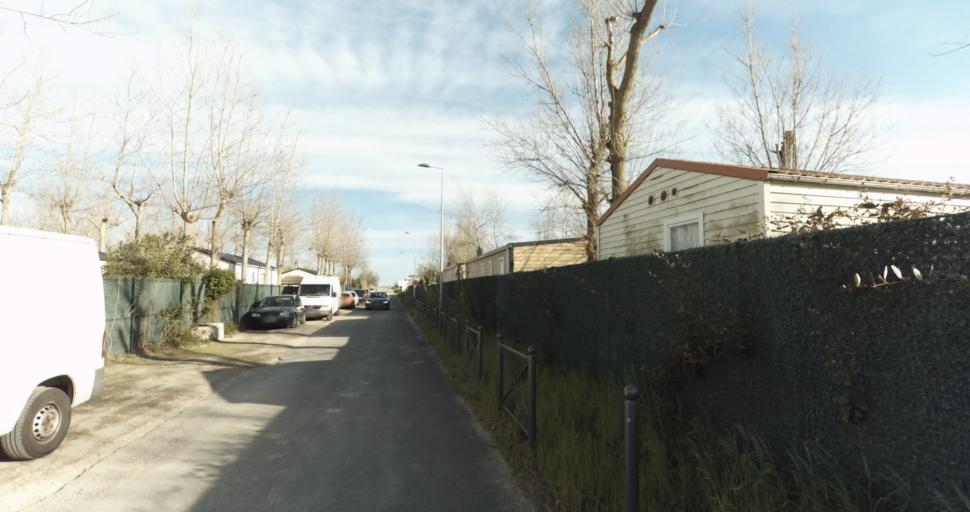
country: FR
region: Languedoc-Roussillon
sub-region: Departement de l'Herault
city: Le Cap d'Agde
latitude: 43.3079
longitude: 3.5424
